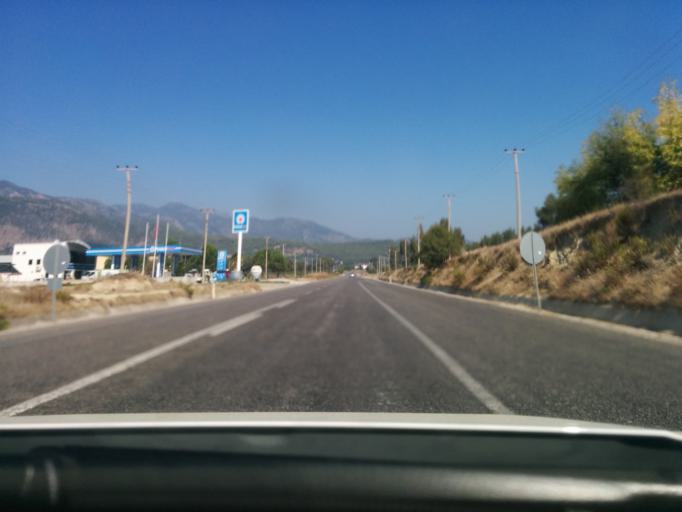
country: TR
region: Mugla
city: Esen
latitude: 36.4533
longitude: 29.2901
